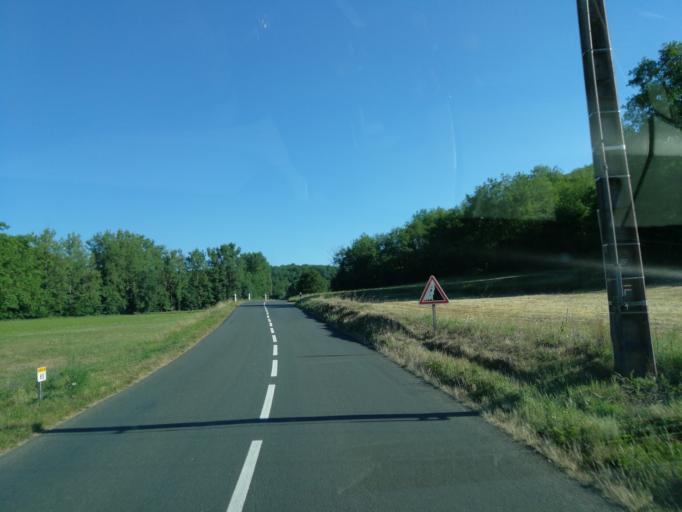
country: FR
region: Midi-Pyrenees
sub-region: Departement du Lot
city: Salviac
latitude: 44.7014
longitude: 1.2960
